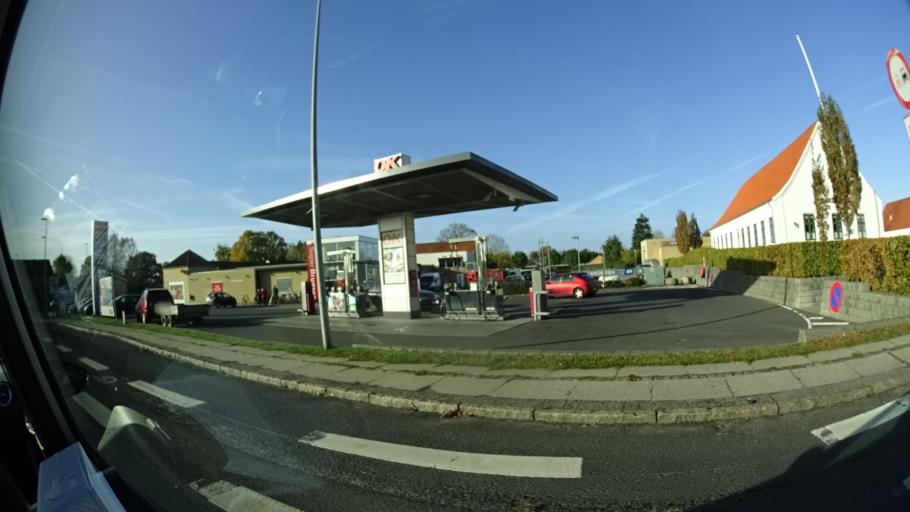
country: DK
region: South Denmark
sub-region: Odense Kommune
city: Hojby
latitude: 55.3323
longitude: 10.4368
